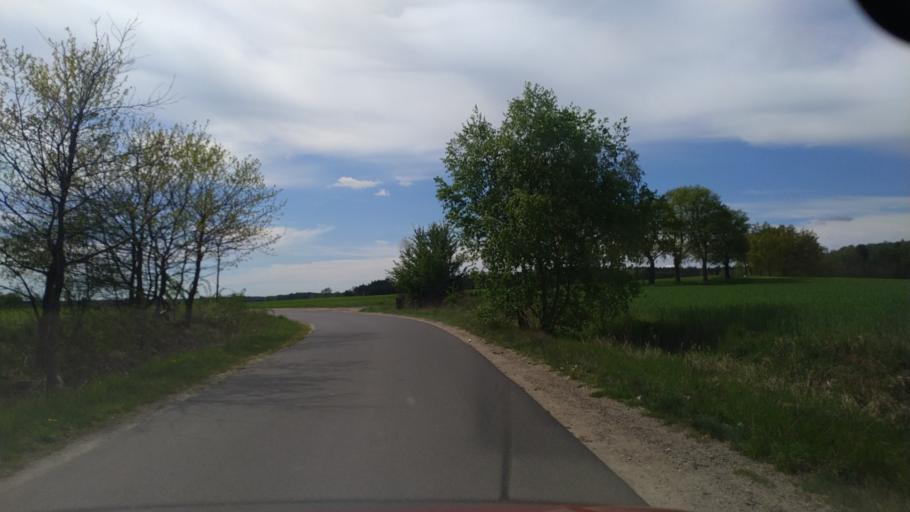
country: PL
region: West Pomeranian Voivodeship
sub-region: Powiat walecki
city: Miroslawiec
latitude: 53.3475
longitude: 16.2545
